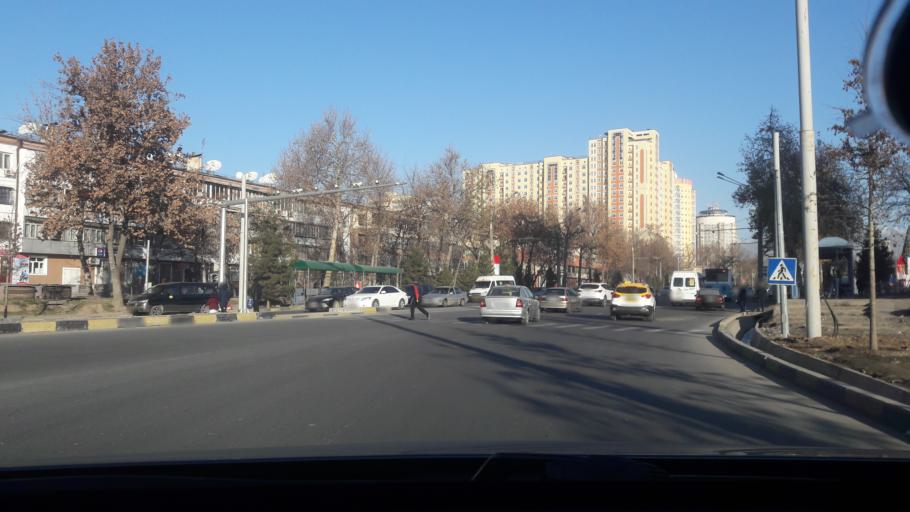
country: TJ
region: Dushanbe
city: Dushanbe
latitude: 38.5589
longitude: 68.7552
